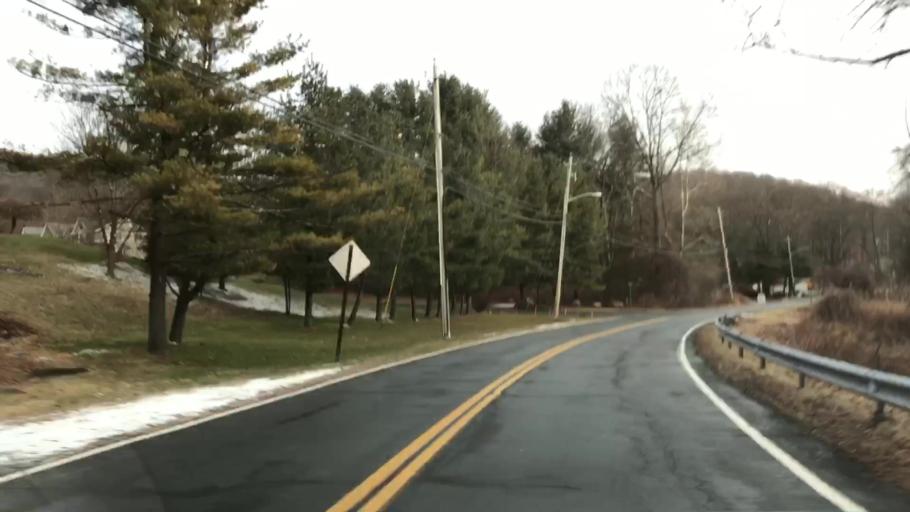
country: US
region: New York
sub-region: Rockland County
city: Thiells
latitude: 41.2270
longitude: -74.0464
